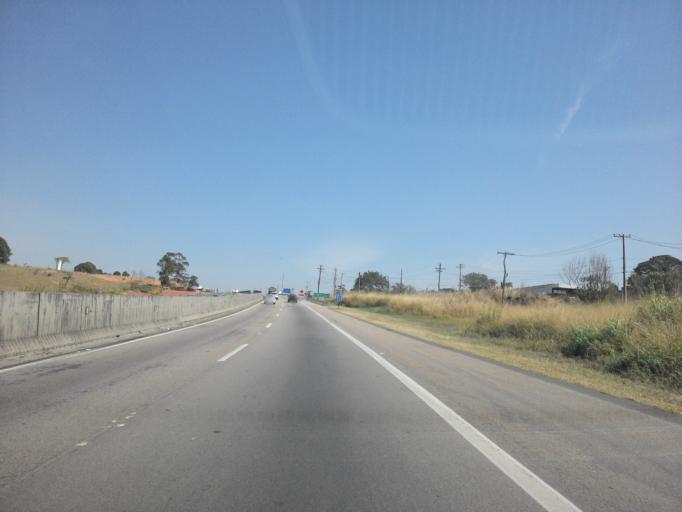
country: BR
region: Sao Paulo
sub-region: Hortolandia
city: Hortolandia
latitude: -22.8852
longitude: -47.1540
